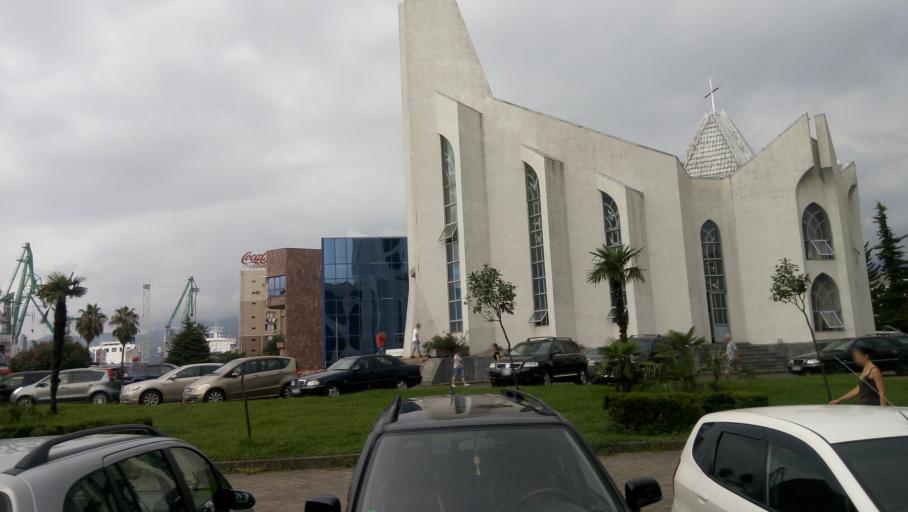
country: GE
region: Ajaria
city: Batumi
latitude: 41.6458
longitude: 41.6493
